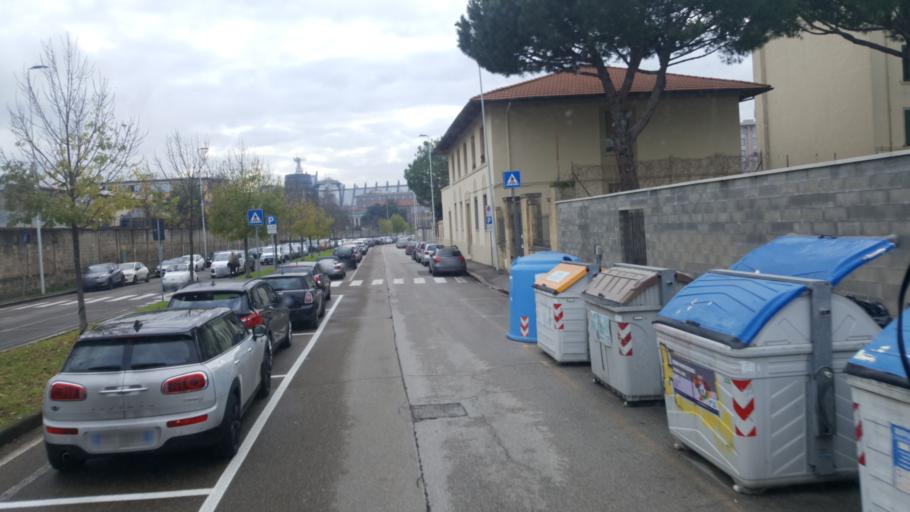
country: IT
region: Tuscany
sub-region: Province of Florence
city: Florence
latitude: 43.8002
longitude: 11.2293
